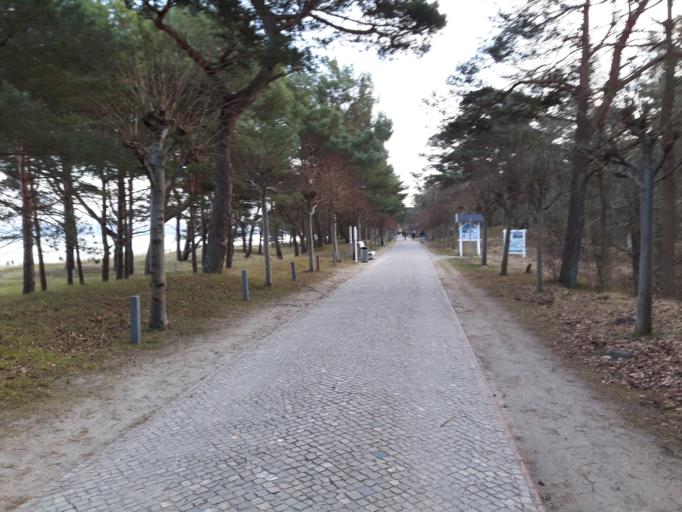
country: DE
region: Mecklenburg-Vorpommern
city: Ostseebad Binz
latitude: 54.4154
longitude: 13.5958
